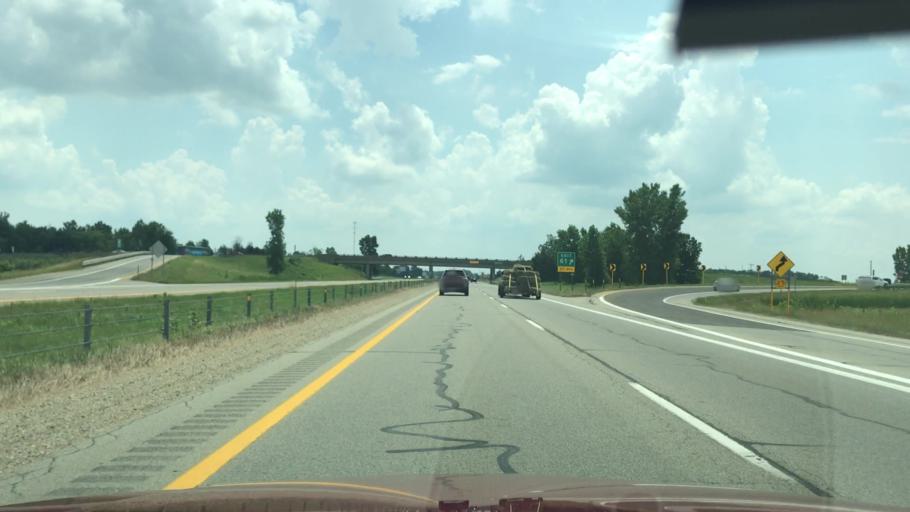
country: US
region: Michigan
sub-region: Allegan County
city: Wayland
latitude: 42.6327
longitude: -85.6624
